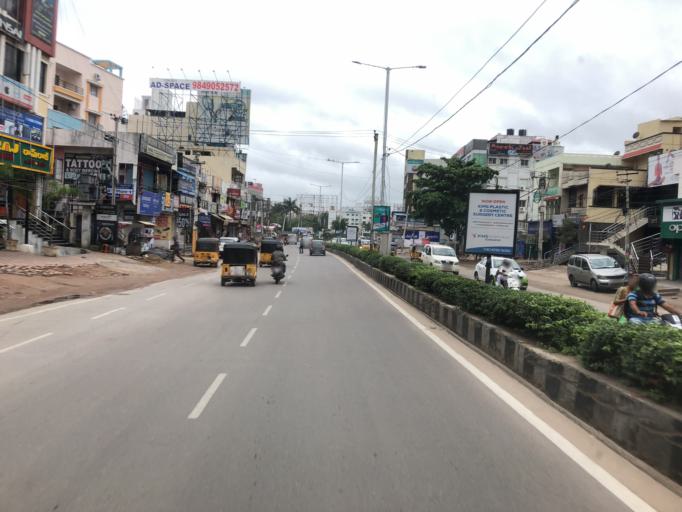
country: IN
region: Telangana
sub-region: Rangareddi
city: Kukatpalli
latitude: 17.4630
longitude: 78.3672
